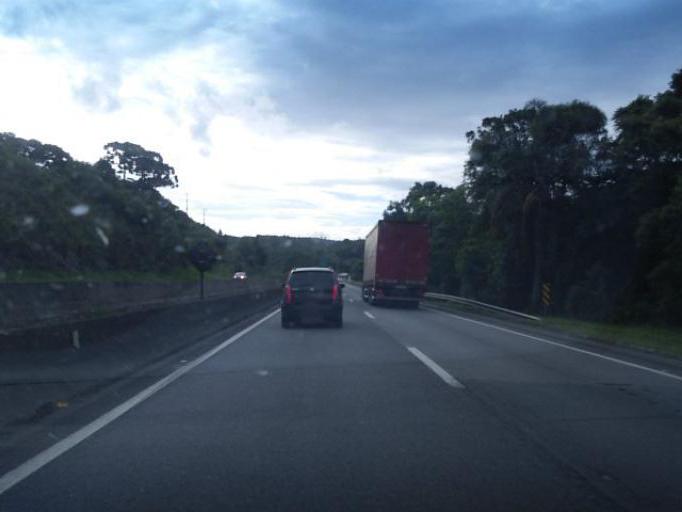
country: BR
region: Parana
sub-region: Campina Grande Do Sul
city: Campina Grande do Sul
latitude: -25.3107
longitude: -49.0060
